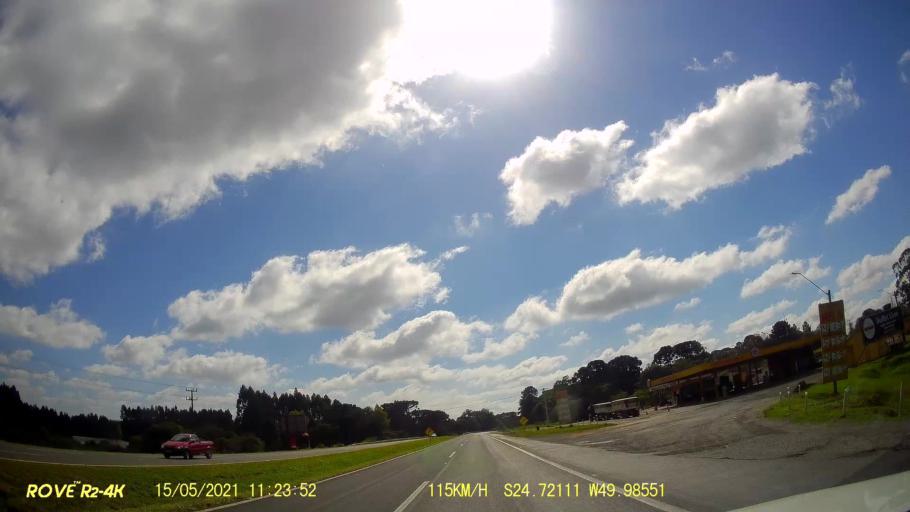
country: BR
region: Parana
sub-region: Castro
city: Castro
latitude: -24.7211
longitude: -49.9854
